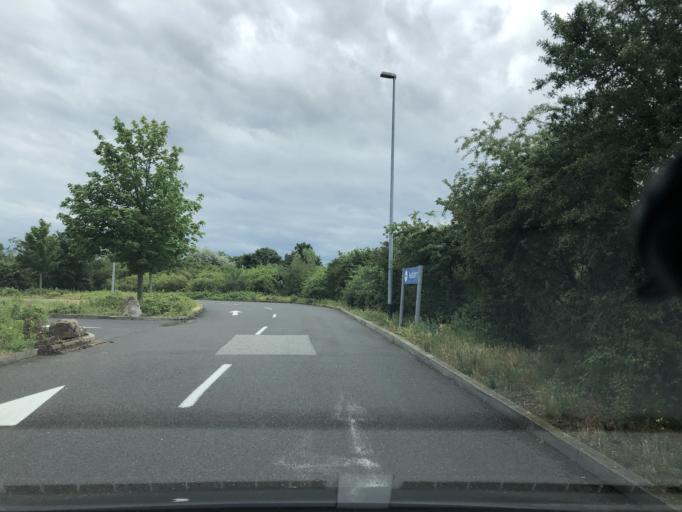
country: DE
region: Hesse
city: Lampertheim
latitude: 49.5552
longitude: 8.4427
